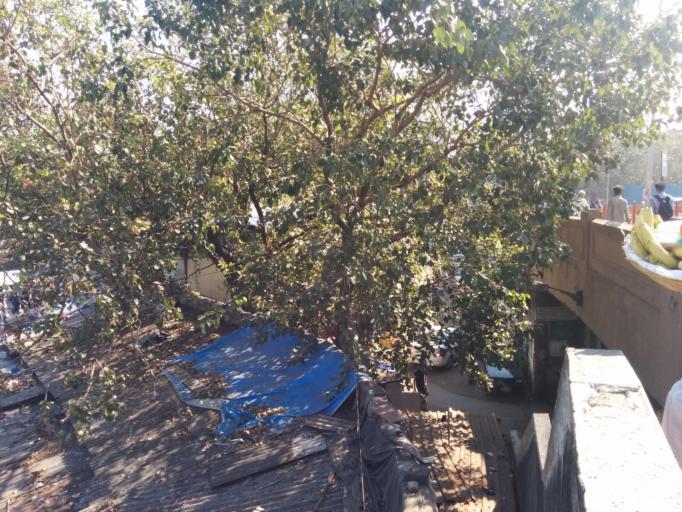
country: IN
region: Maharashtra
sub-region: Mumbai Suburban
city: Mumbai
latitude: 18.9821
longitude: 72.8247
